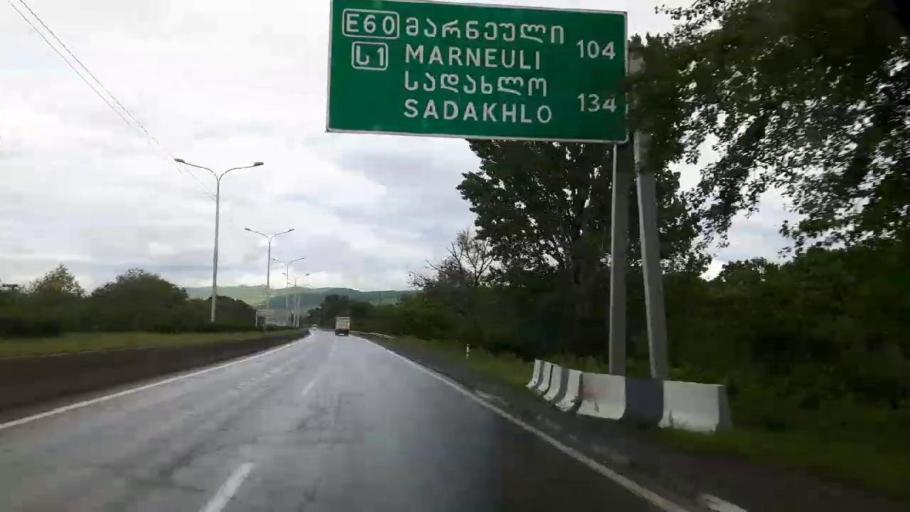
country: GE
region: Shida Kartli
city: Kaspi
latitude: 41.9115
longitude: 44.5651
